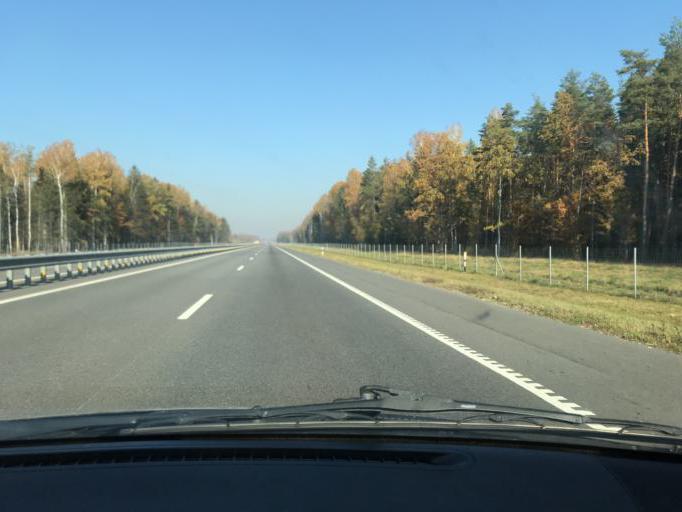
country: BY
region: Minsk
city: Slutsk
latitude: 53.2399
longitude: 27.5504
